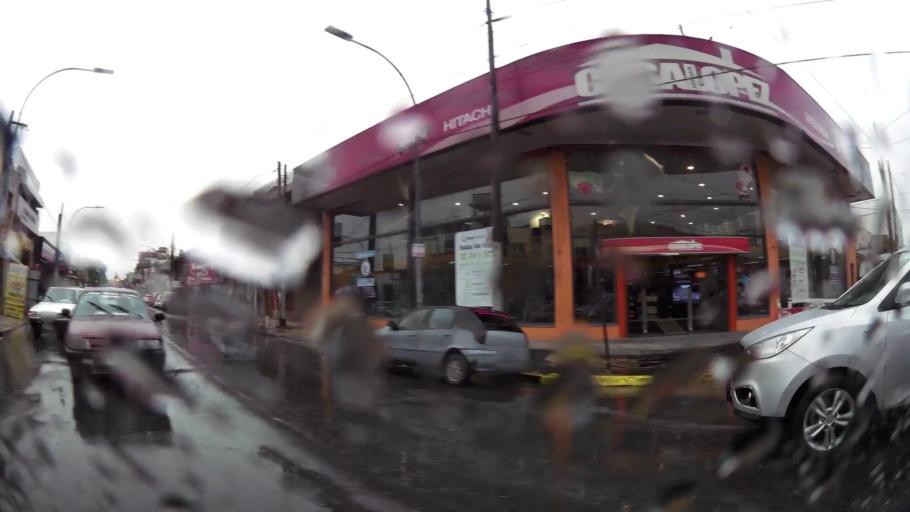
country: AR
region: Buenos Aires
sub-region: Partido de Lanus
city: Lanus
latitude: -34.7062
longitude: -58.4173
